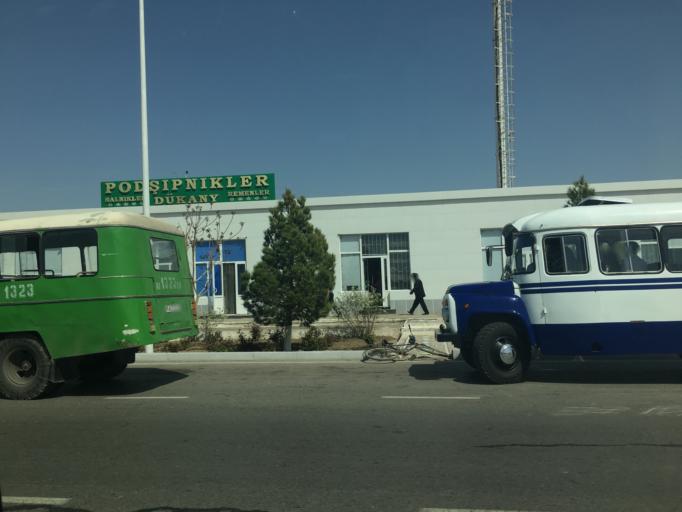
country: TM
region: Lebap
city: Turkmenabat
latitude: 39.0194
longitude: 63.5982
